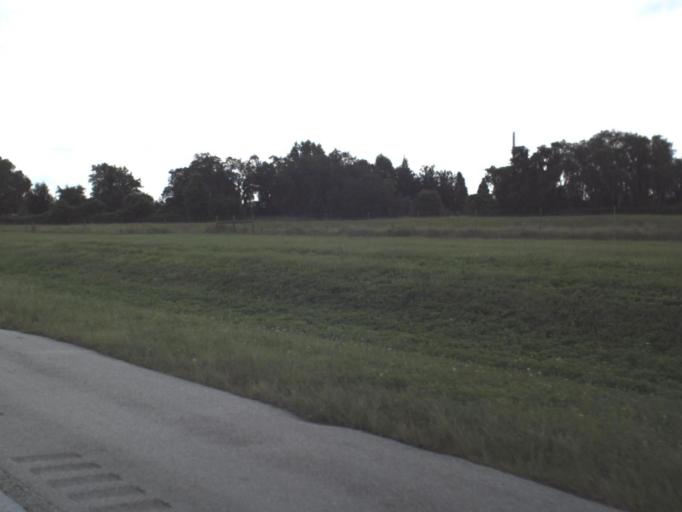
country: US
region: Florida
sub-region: Polk County
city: Gibsonia
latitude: 28.1269
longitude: -81.9234
